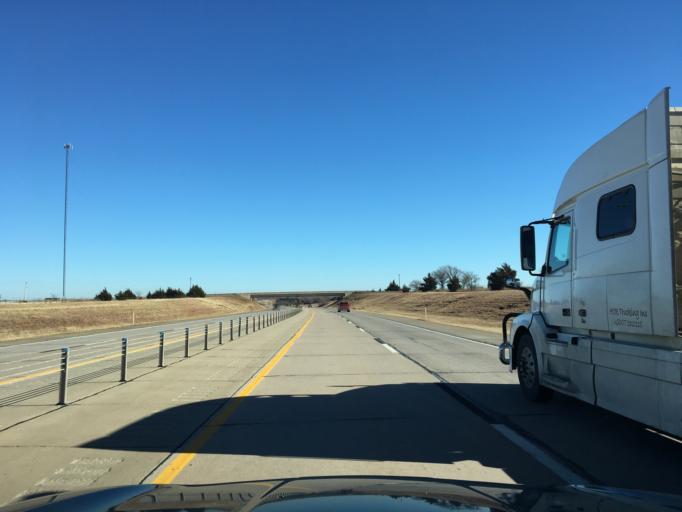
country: US
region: Oklahoma
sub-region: Pawnee County
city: Pawnee
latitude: 36.2249
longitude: -96.8935
